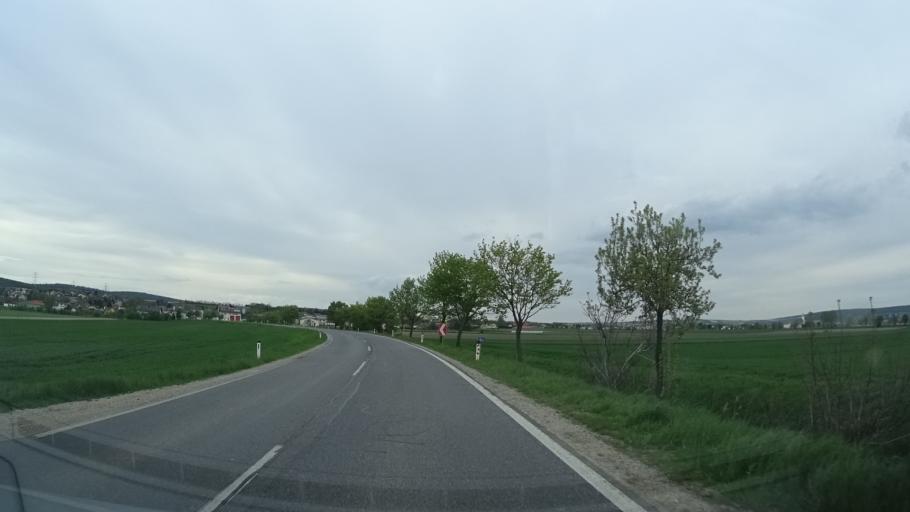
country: AT
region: Lower Austria
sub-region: Politischer Bezirk Korneuburg
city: Harmannsdorf
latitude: 48.3757
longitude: 16.3611
